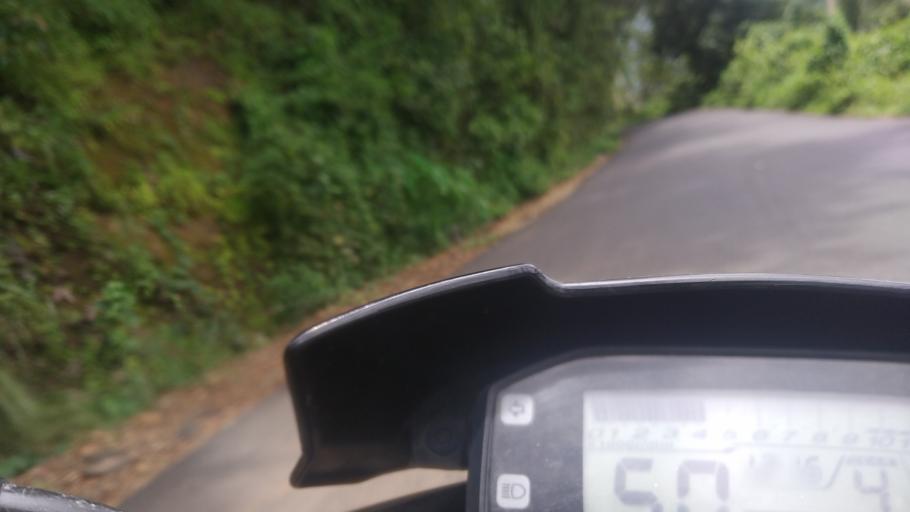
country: IN
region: Kerala
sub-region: Idukki
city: Munnar
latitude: 10.0162
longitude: 77.0124
